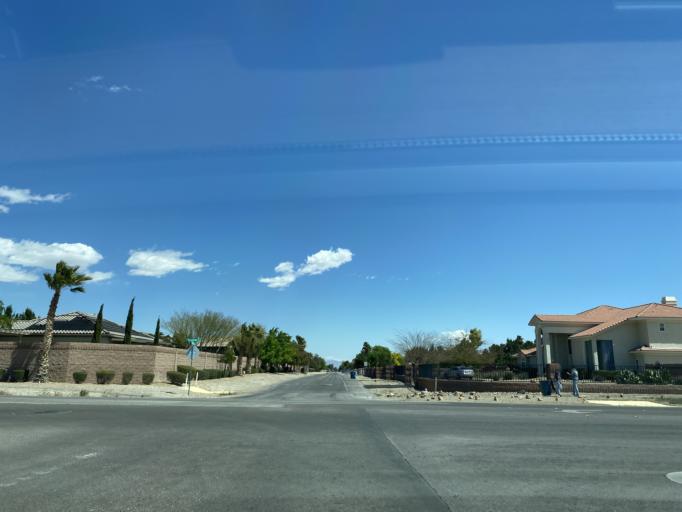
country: US
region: Nevada
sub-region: Clark County
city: North Las Vegas
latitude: 36.3016
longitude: -115.2424
